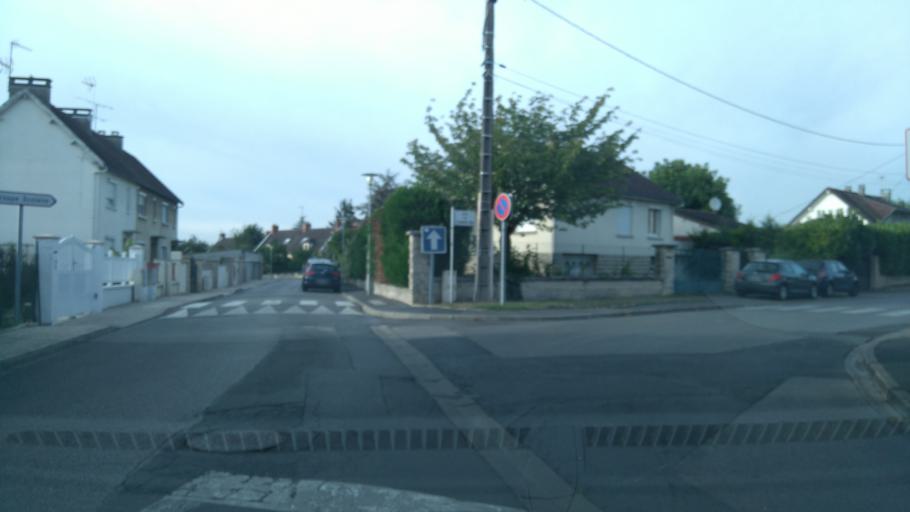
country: FR
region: Picardie
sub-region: Departement de l'Oise
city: Saint-Maximin
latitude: 49.2220
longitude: 2.4459
